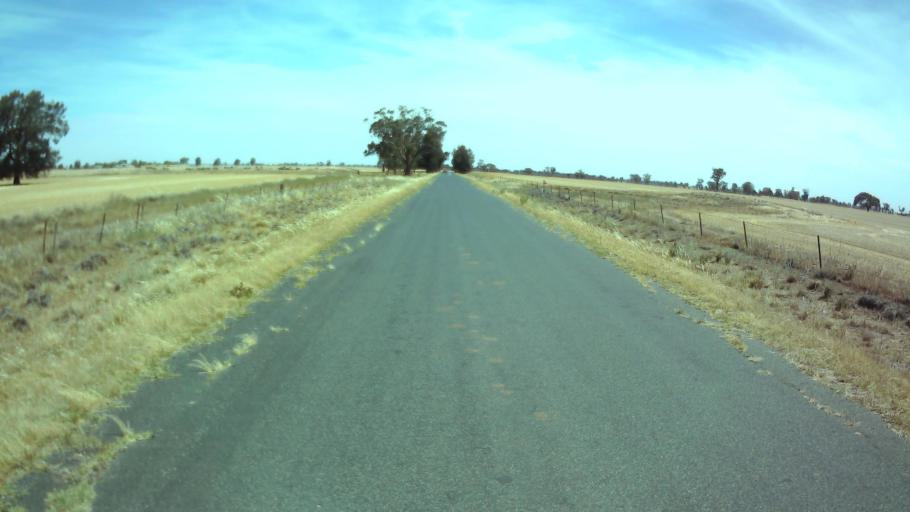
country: AU
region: New South Wales
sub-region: Weddin
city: Grenfell
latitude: -33.9260
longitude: 147.7632
